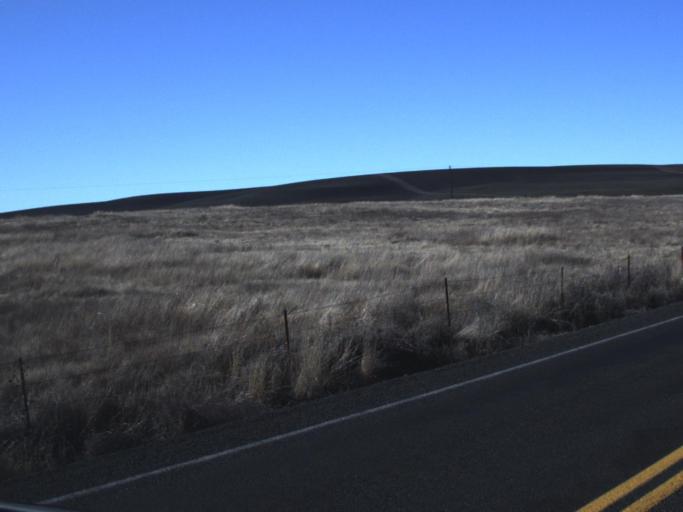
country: US
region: Washington
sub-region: Adams County
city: Ritzville
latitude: 46.7921
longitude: -118.2926
